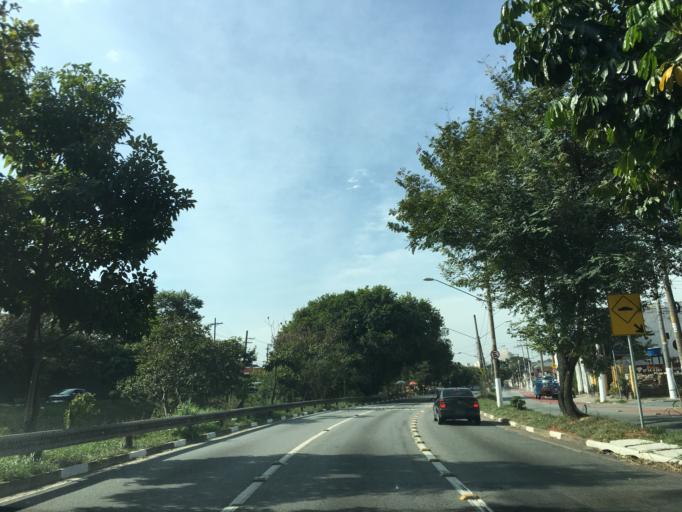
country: BR
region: Sao Paulo
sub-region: Osasco
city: Osasco
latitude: -23.5707
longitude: -46.7630
